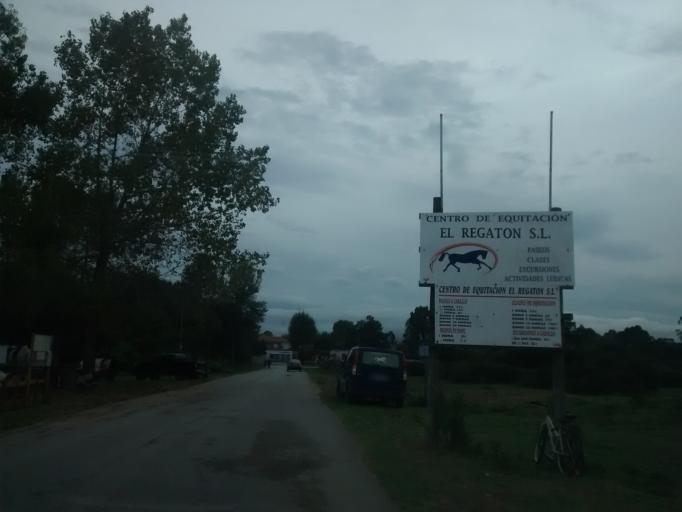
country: ES
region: Cantabria
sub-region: Provincia de Cantabria
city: Colindres
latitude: 43.4162
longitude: -3.4463
